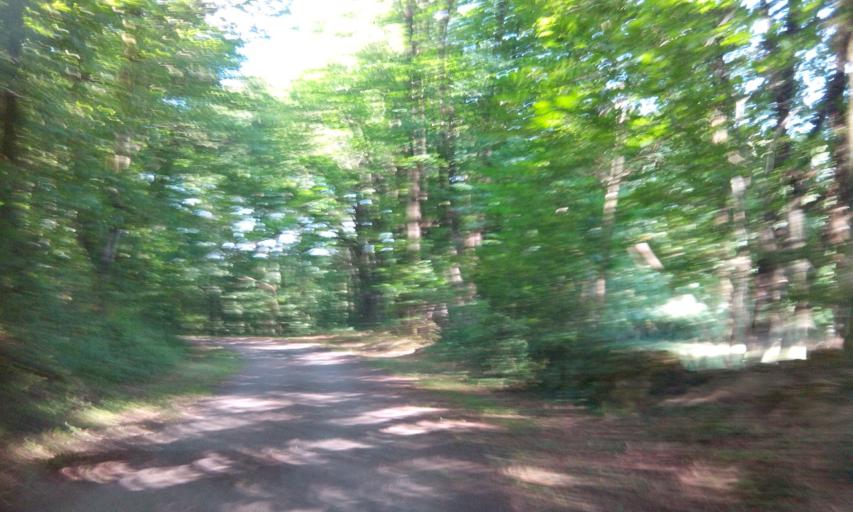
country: FR
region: Limousin
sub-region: Departement de la Haute-Vienne
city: Saint-Leonard-de-Noblat
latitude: 45.8073
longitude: 1.4829
